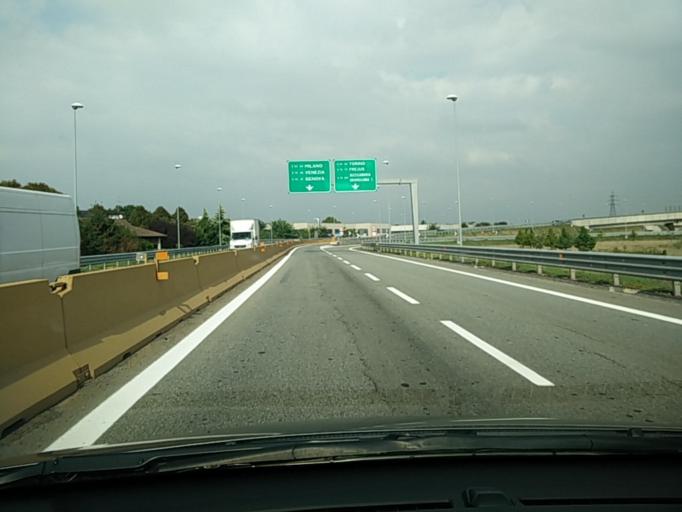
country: IT
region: Lombardy
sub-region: Citta metropolitana di Milano
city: Mesero
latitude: 45.4893
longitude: 8.8586
